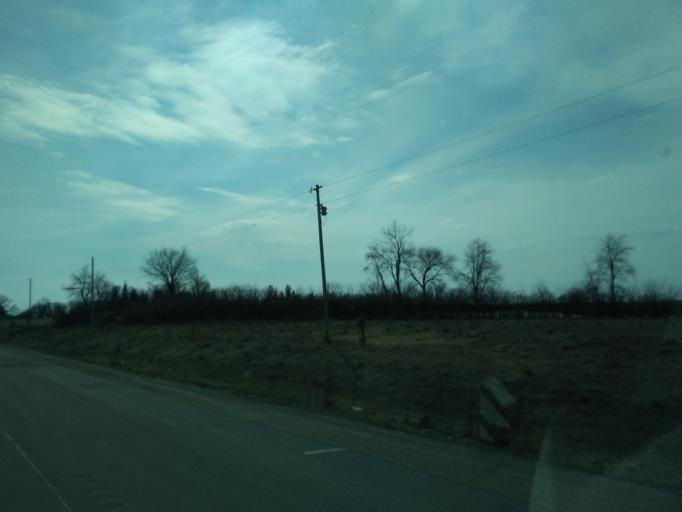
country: US
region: Minnesota
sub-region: Fillmore County
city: Harmony
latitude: 43.5144
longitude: -91.8698
